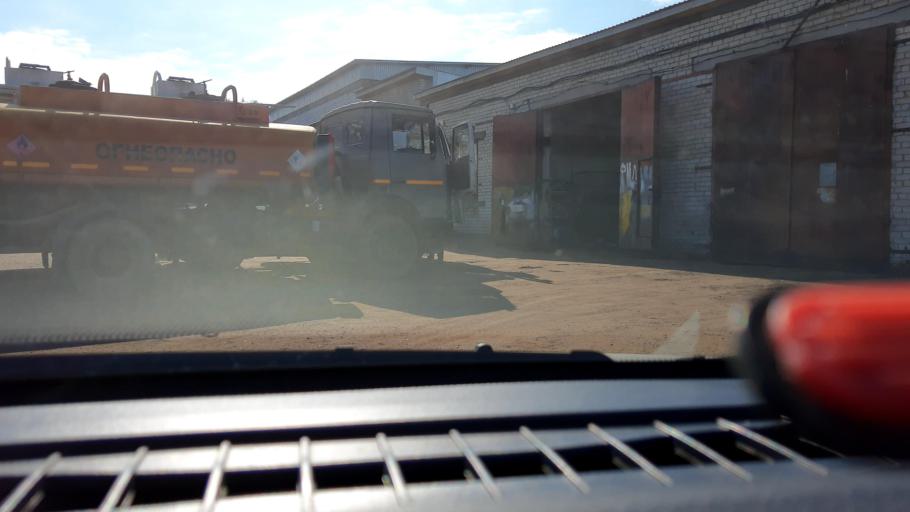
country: RU
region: Nizjnij Novgorod
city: Kstovo
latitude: 56.1988
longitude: 44.1527
